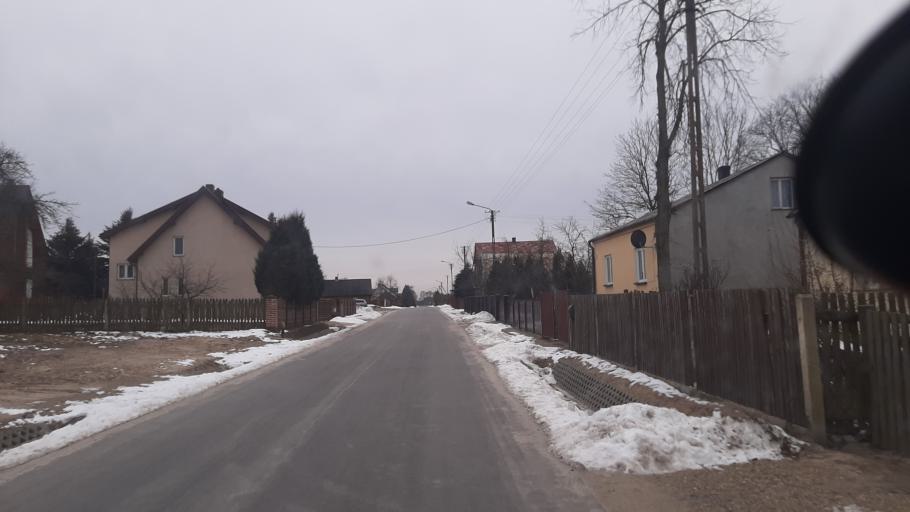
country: PL
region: Lublin Voivodeship
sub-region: Powiat lubartowski
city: Kamionka
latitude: 51.5166
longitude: 22.4737
